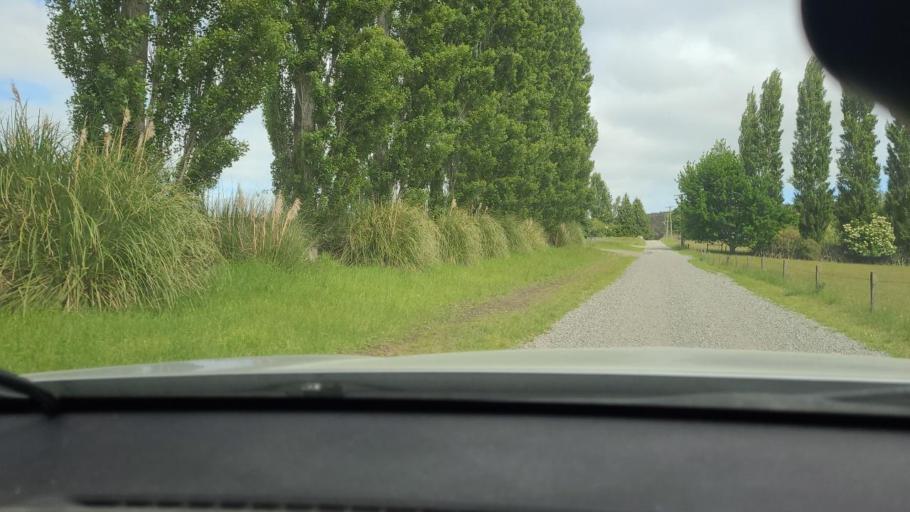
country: NZ
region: Southland
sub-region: Southland District
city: Winton
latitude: -45.9375
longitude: 168.0347
